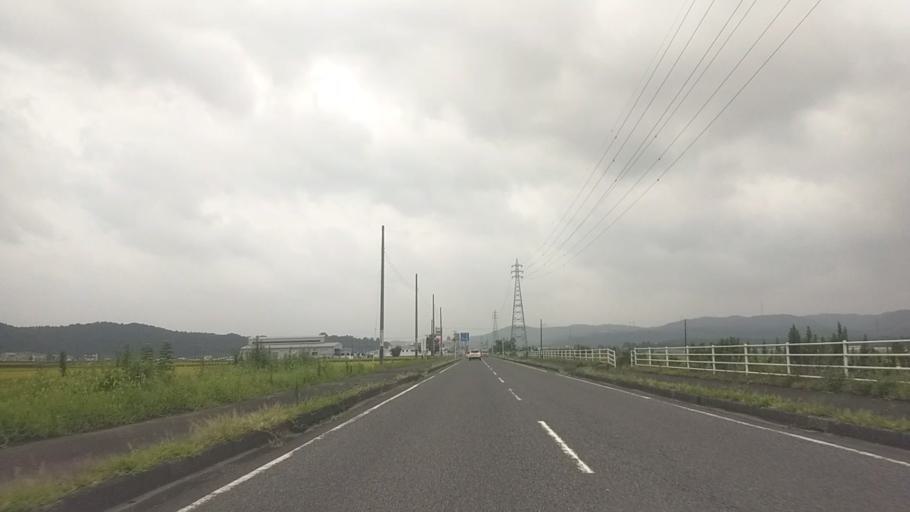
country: JP
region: Chiba
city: Kisarazu
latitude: 35.3337
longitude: 140.0549
